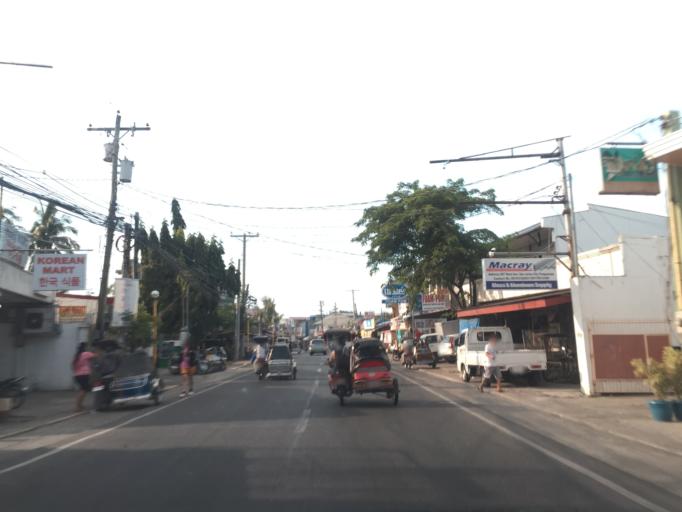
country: PH
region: Ilocos
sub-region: Province of Pangasinan
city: Bolingit
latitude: 15.9301
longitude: 120.3481
